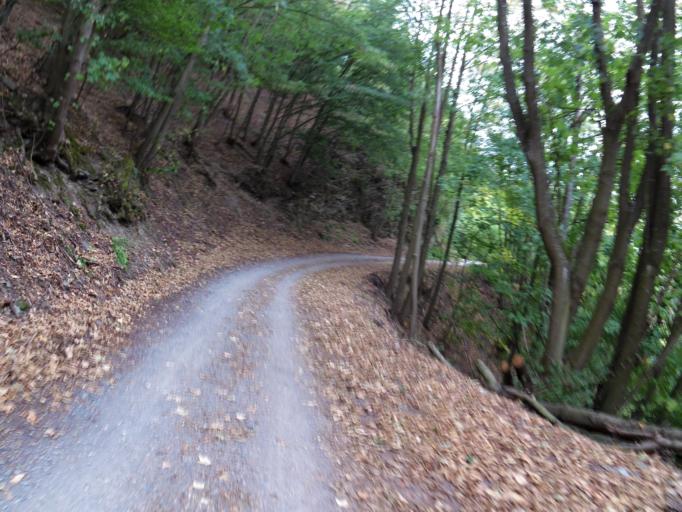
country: DE
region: North Rhine-Westphalia
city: Heimbach
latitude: 50.6258
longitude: 6.3989
